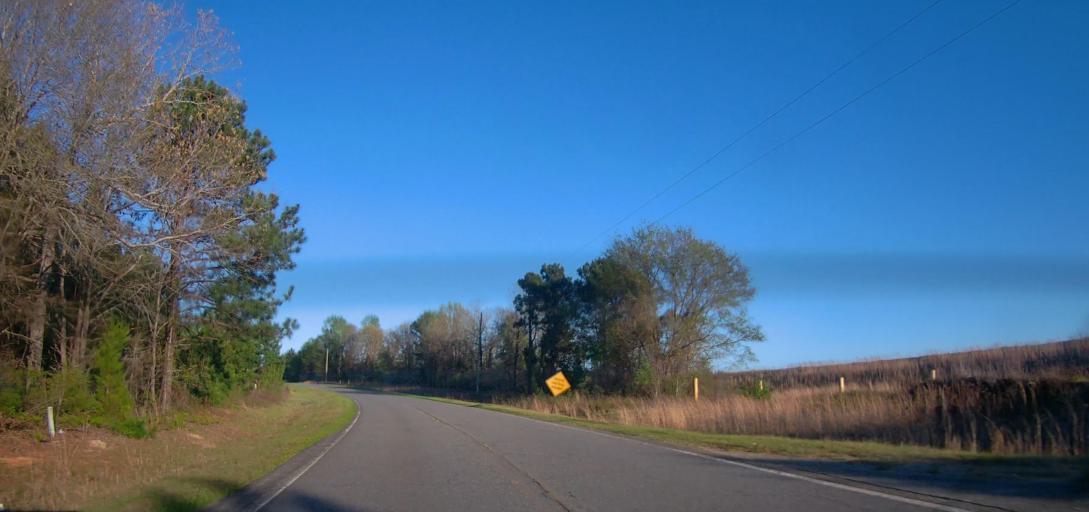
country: US
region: Georgia
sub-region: Wilkinson County
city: Gordon
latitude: 32.8713
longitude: -83.2436
